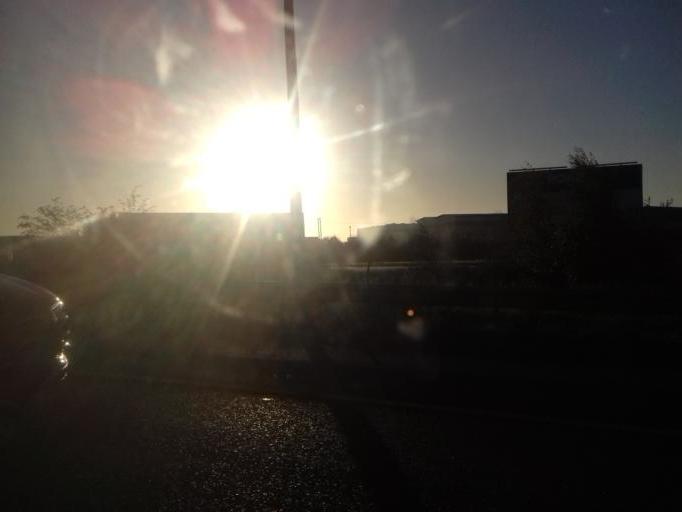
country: IE
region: Leinster
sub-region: Dublin City
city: Finglas
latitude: 53.4012
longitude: -6.3181
